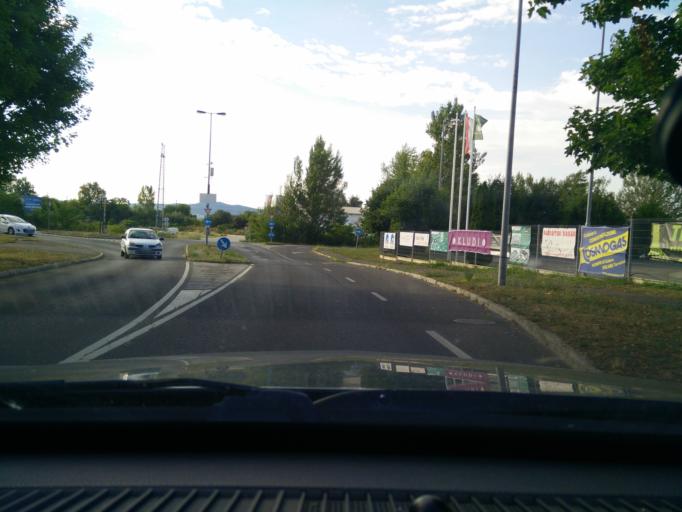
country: HU
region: Pest
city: Toeroekbalint
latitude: 47.4459
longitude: 18.8942
